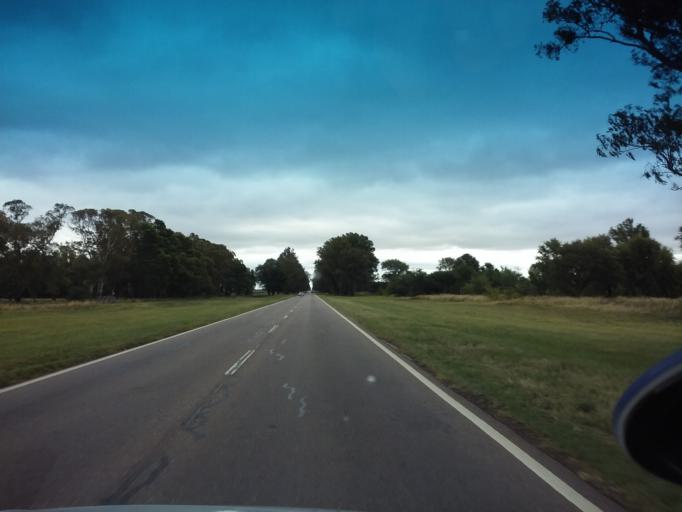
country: AR
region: La Pampa
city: Anguil
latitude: -36.5674
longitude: -64.1342
